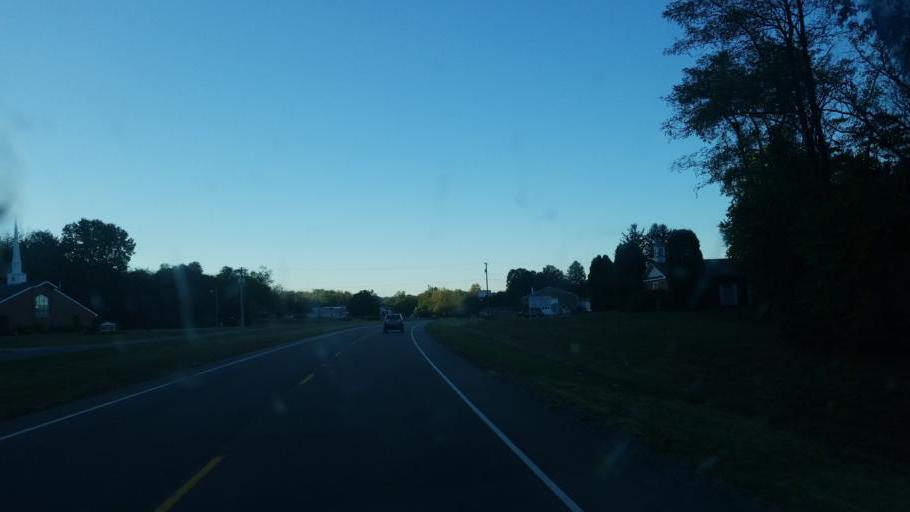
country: US
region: Ohio
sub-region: Coshocton County
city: Coshocton
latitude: 40.2912
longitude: -81.8869
